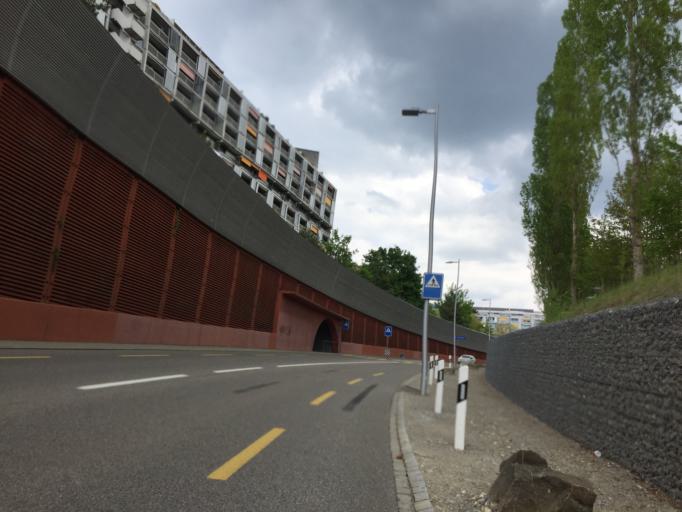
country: CH
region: Bern
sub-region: Bern-Mittelland District
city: Wohlen
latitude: 46.9482
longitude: 7.3738
